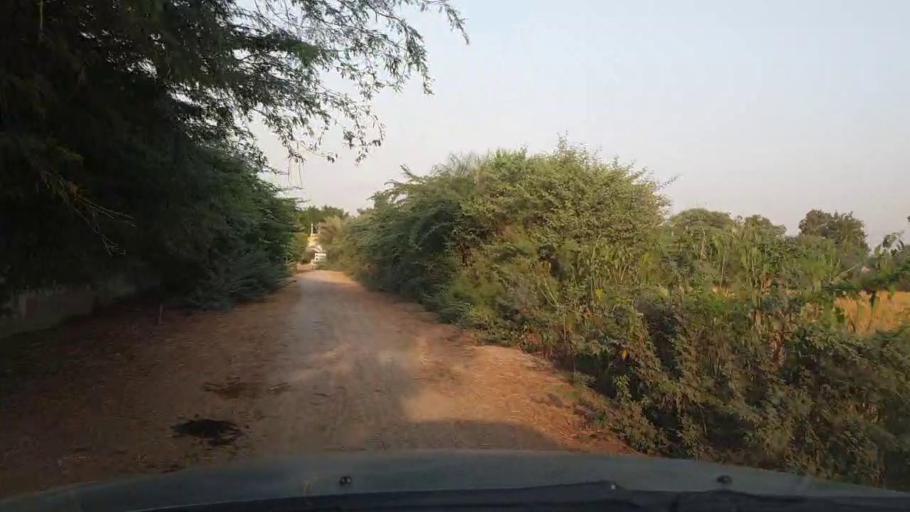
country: PK
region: Sindh
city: Tando Muhammad Khan
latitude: 24.9990
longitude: 68.4363
